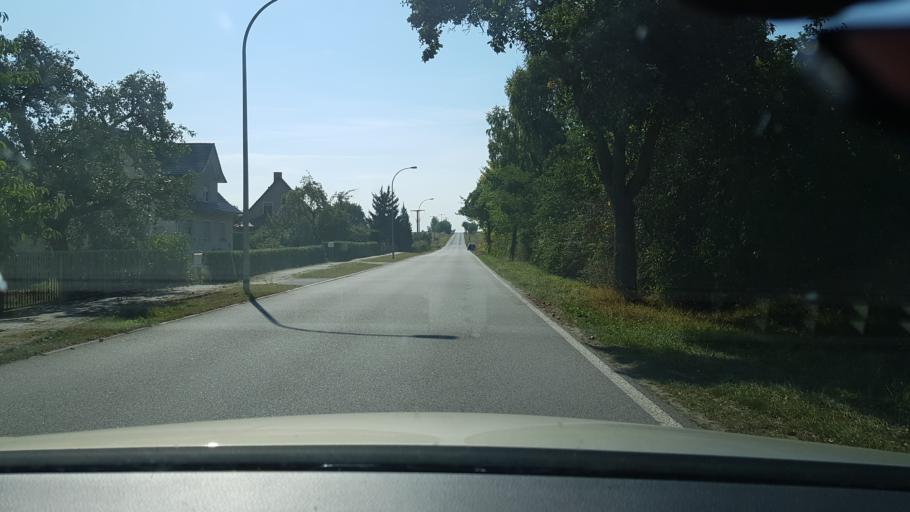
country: DE
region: Brandenburg
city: Lawitz
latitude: 52.1247
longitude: 14.5902
